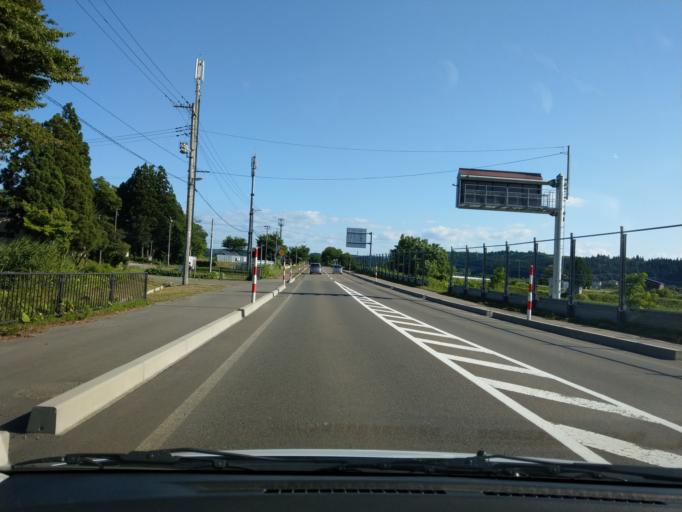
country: JP
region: Akita
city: Takanosu
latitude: 40.2003
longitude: 140.3962
